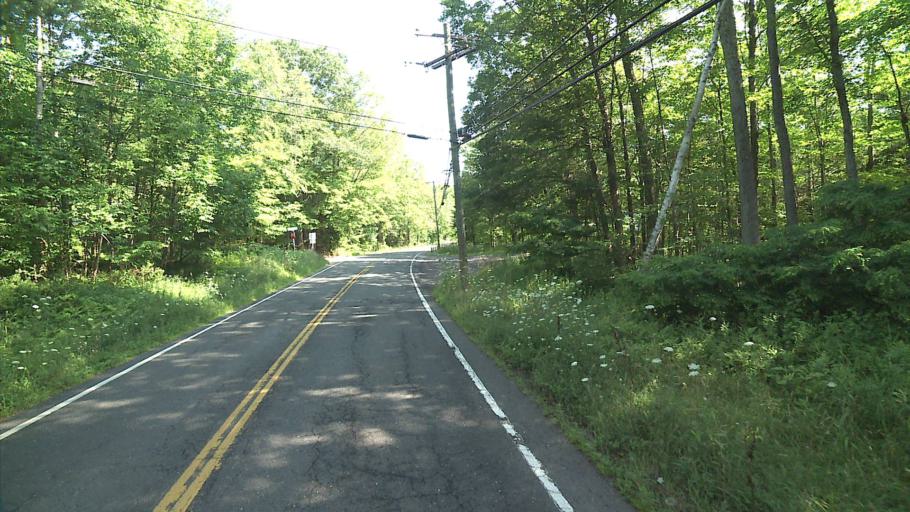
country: US
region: Connecticut
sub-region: Litchfield County
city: Winsted
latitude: 41.9742
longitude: -73.1053
